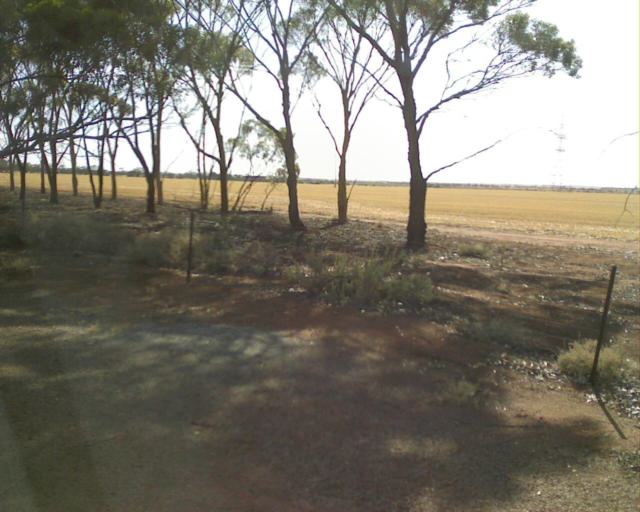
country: AU
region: Western Australia
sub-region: Irwin
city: Dongara
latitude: -29.5363
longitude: 115.7688
